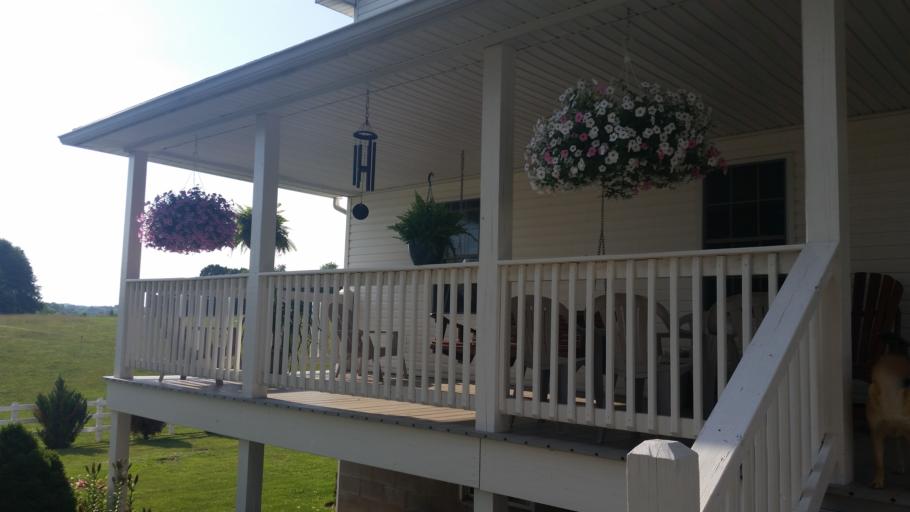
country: US
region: Ohio
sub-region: Gallia County
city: Gallipolis
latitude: 38.8309
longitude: -82.3208
